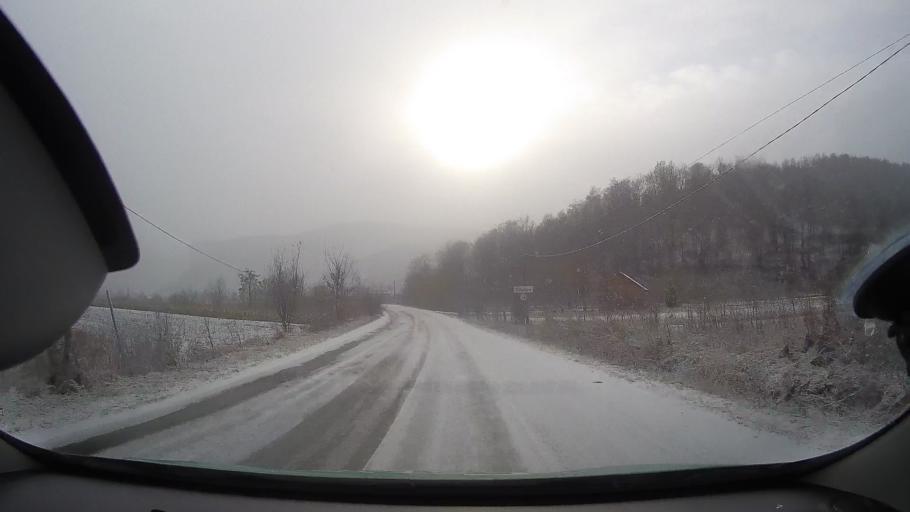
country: RO
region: Alba
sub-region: Comuna Rimetea
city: Rimetea
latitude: 46.3940
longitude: 23.5603
